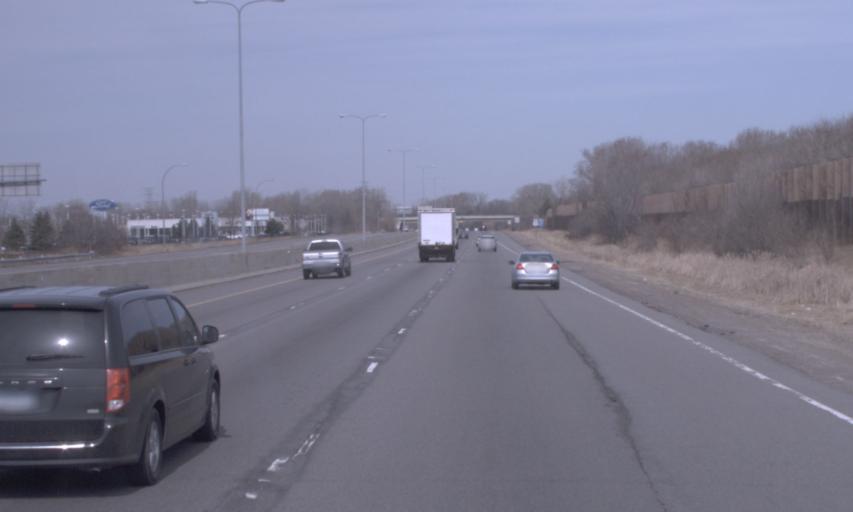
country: US
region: Minnesota
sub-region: Anoka County
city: Coon Rapids
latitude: 45.1571
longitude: -93.2791
